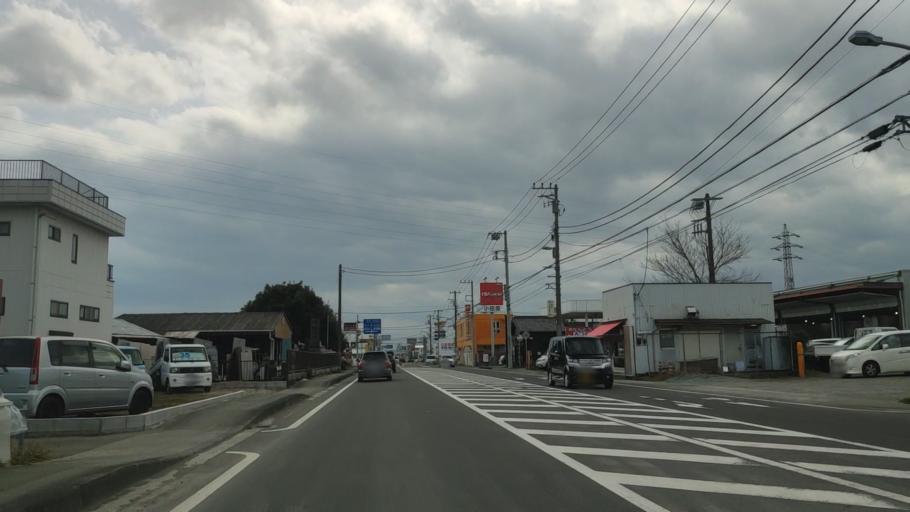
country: JP
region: Kanagawa
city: Odawara
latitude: 35.3000
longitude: 139.1668
